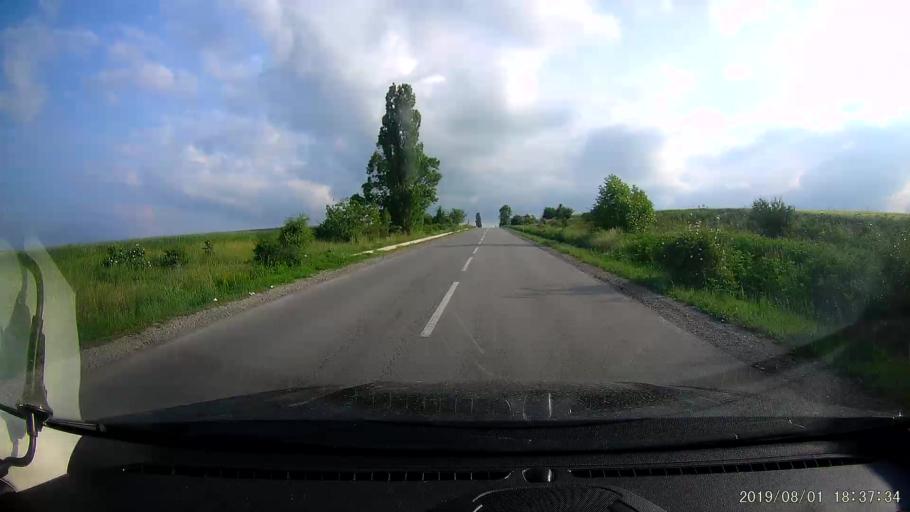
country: BG
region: Shumen
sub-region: Obshtina Khitrino
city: Gara Khitrino
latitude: 43.4183
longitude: 26.9287
